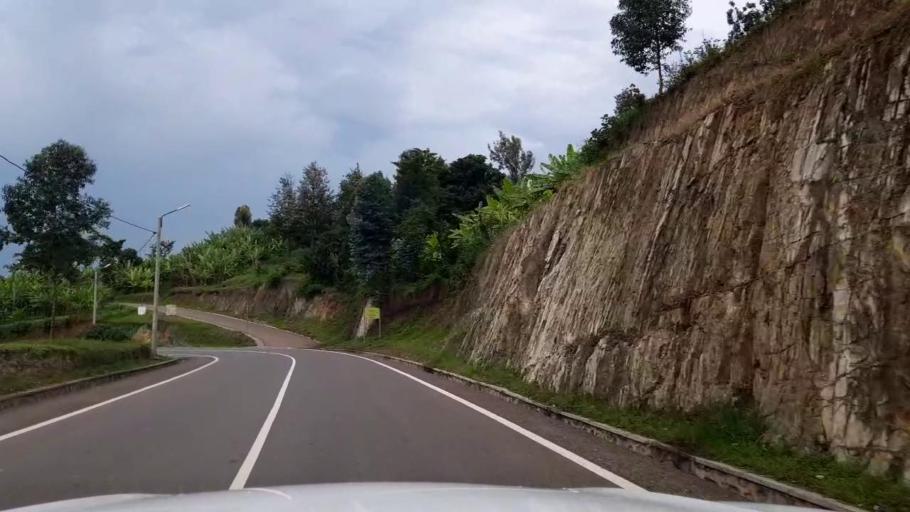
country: RW
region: Western Province
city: Kibuye
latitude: -2.0391
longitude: 29.4046
